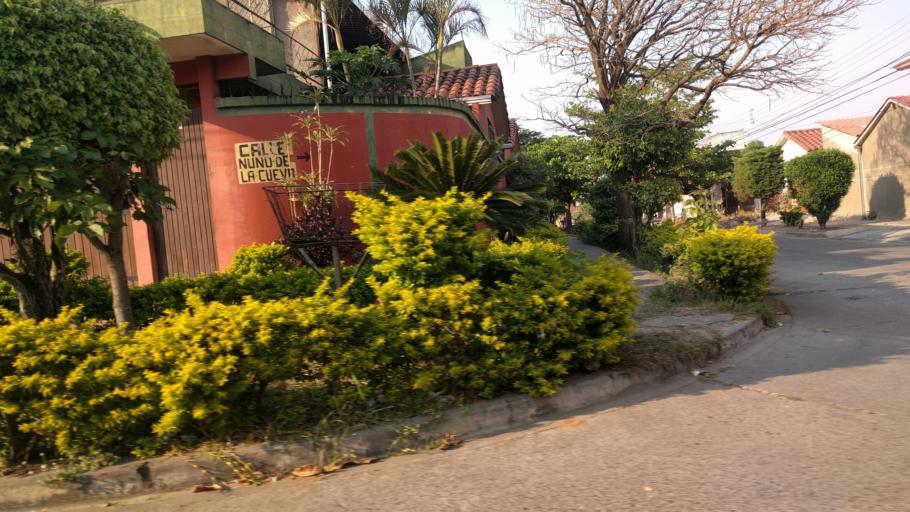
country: BO
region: Santa Cruz
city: Santa Cruz de la Sierra
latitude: -17.8018
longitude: -63.1879
